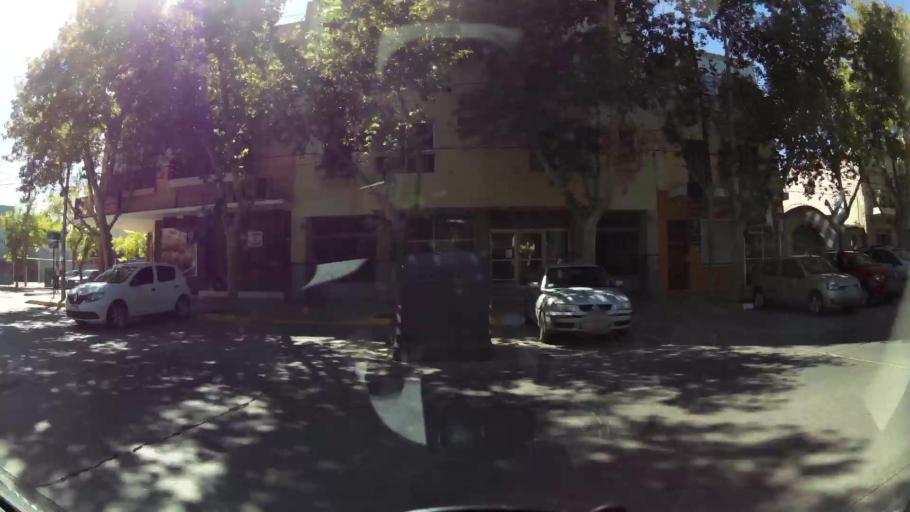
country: AR
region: San Juan
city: San Juan
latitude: -31.5378
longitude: -68.5327
